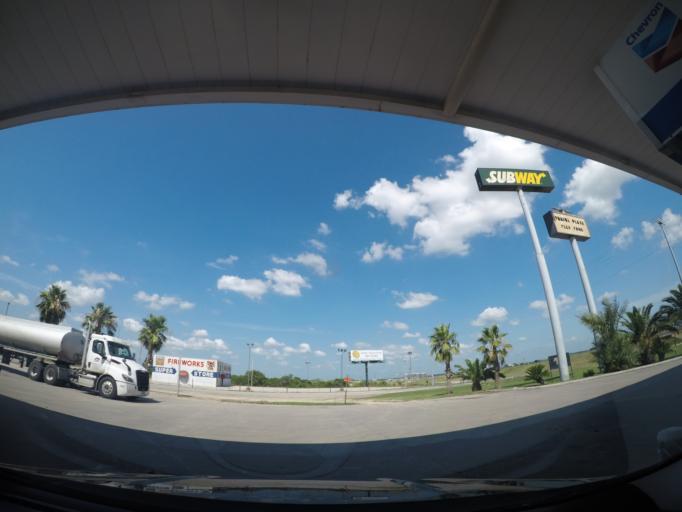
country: US
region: Texas
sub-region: Guadalupe County
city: McQueeney
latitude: 29.5415
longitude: -98.0733
